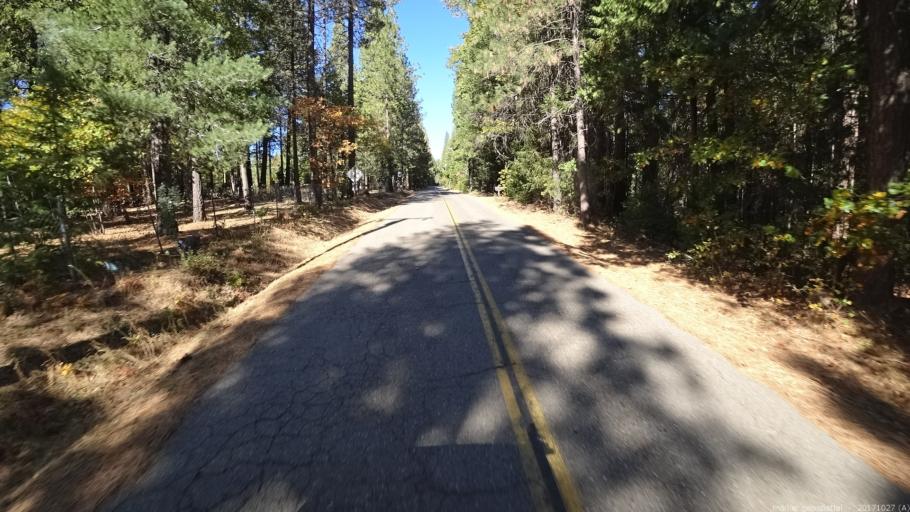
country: US
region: California
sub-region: Shasta County
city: Shingletown
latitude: 40.7209
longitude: -121.9339
